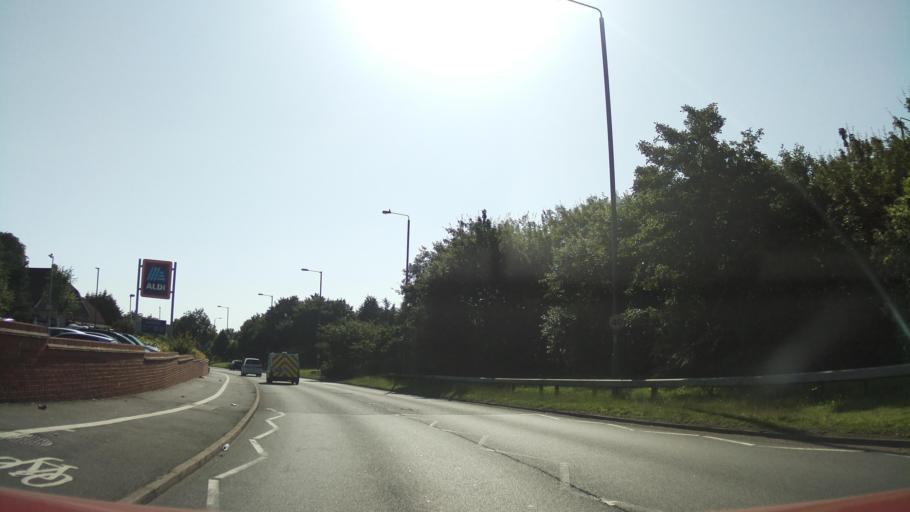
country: GB
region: England
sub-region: Derby
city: Derby
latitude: 52.9124
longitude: -1.5157
